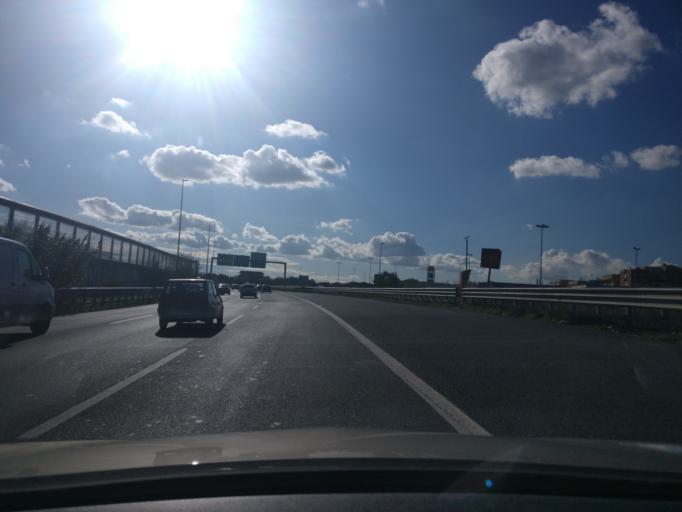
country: IT
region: Latium
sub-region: Citta metropolitana di Roma Capitale
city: Ciampino
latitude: 41.8324
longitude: 12.5848
